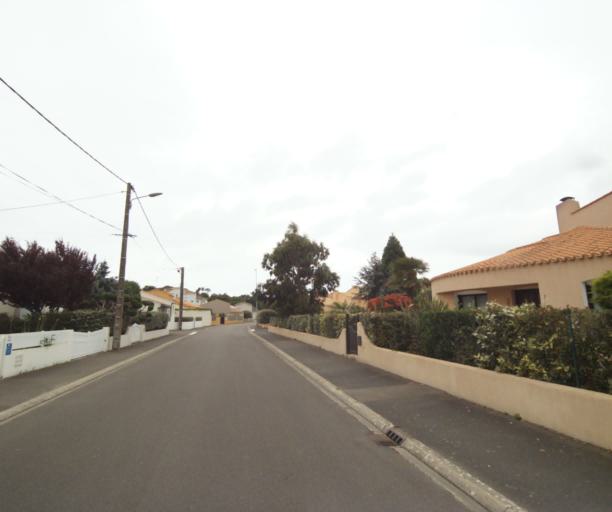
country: FR
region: Pays de la Loire
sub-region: Departement de la Vendee
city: Chateau-d'Olonne
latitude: 46.4896
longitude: -1.7585
